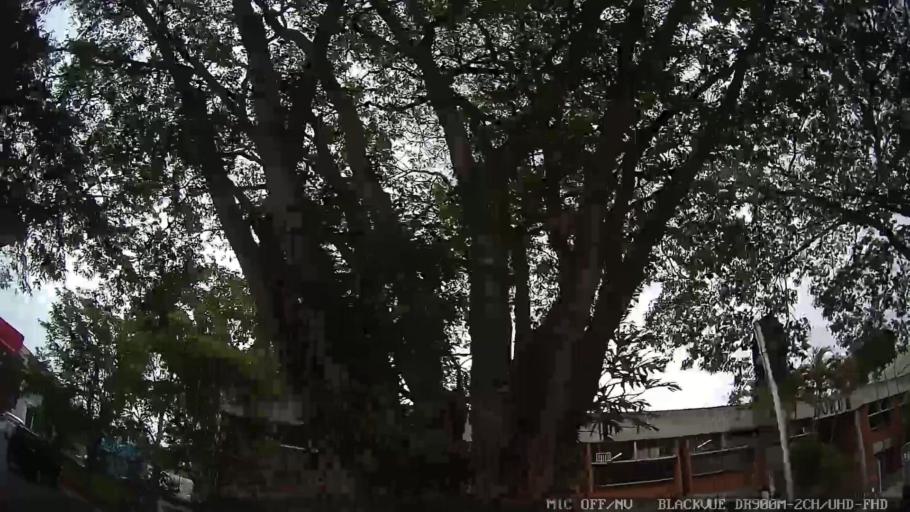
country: BR
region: Sao Paulo
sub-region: Braganca Paulista
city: Braganca Paulista
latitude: -22.9591
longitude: -46.5450
